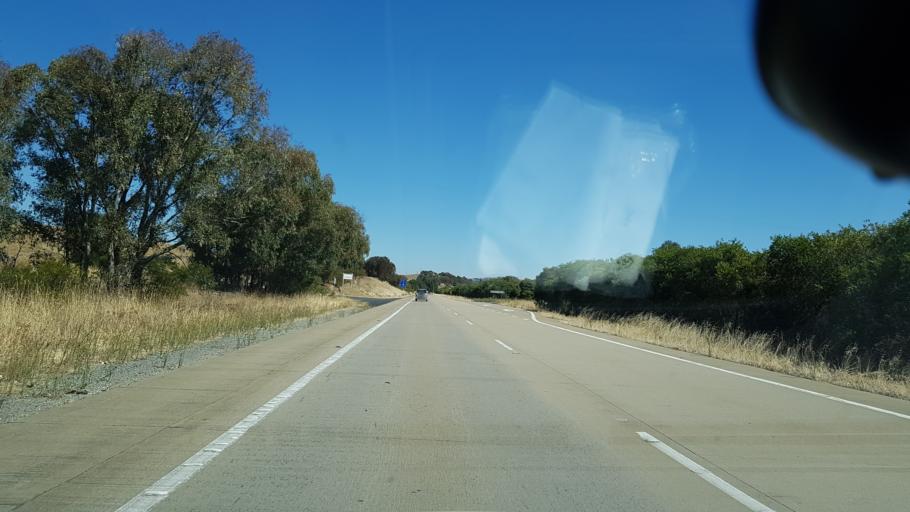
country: AU
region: New South Wales
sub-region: Gundagai
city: Gundagai
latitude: -34.8185
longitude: 148.3830
